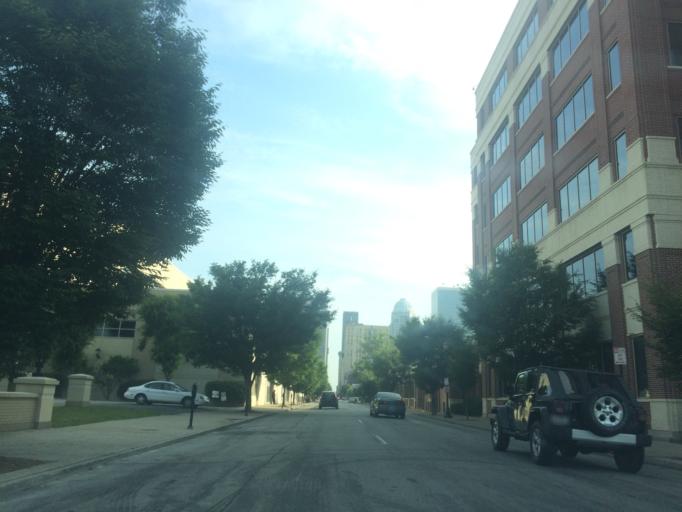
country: US
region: Kentucky
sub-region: Jefferson County
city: Louisville
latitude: 38.2464
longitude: -85.7600
